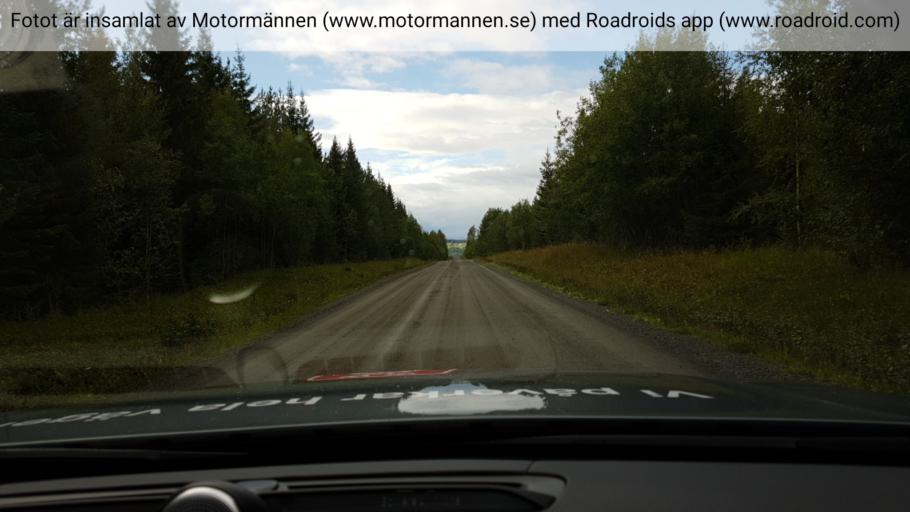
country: SE
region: Jaemtland
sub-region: OEstersunds Kommun
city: Lit
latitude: 63.6783
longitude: 14.8193
